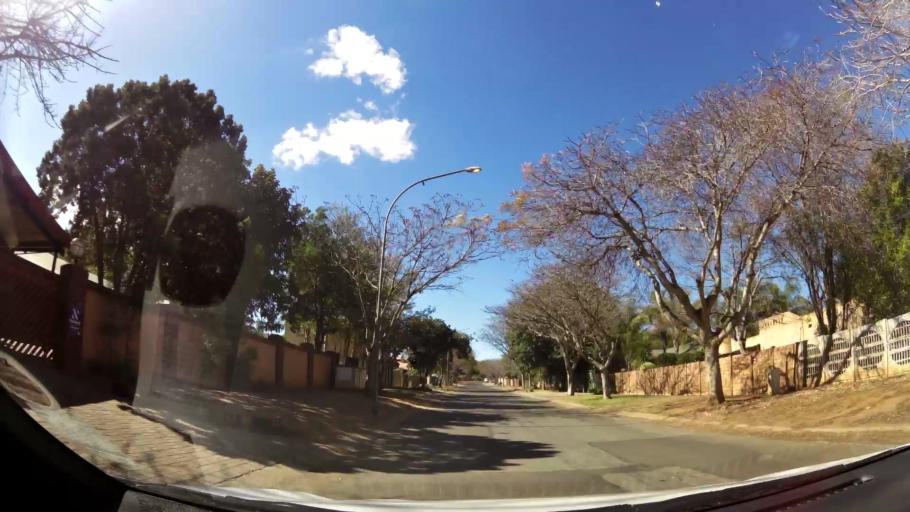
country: ZA
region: Limpopo
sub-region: Capricorn District Municipality
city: Polokwane
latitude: -23.9071
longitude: 29.4791
